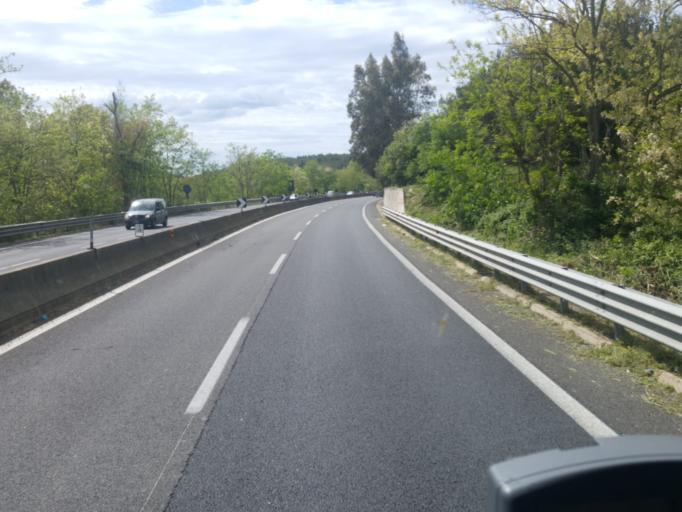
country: IT
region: Latium
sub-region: Citta metropolitana di Roma Capitale
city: Ara Nova
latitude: 41.8970
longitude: 12.2821
